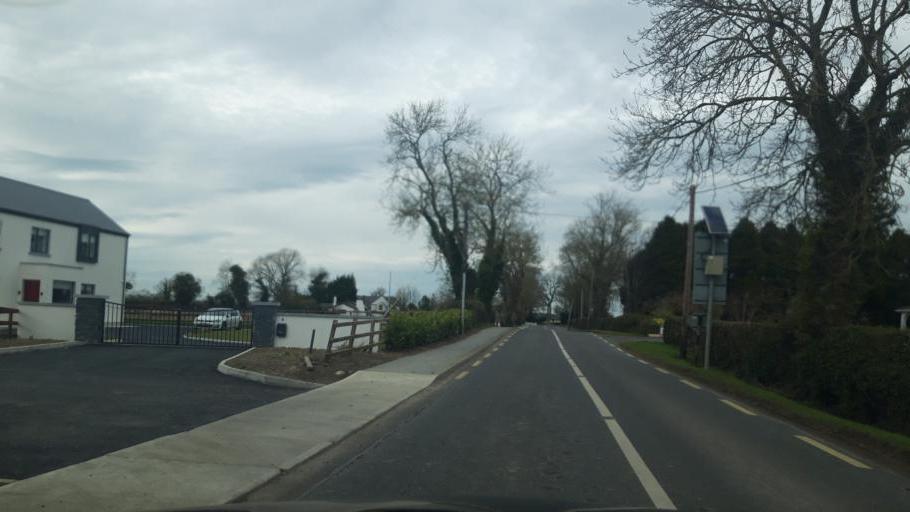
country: IE
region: Leinster
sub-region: Kildare
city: Clane
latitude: 53.3345
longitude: -6.6761
